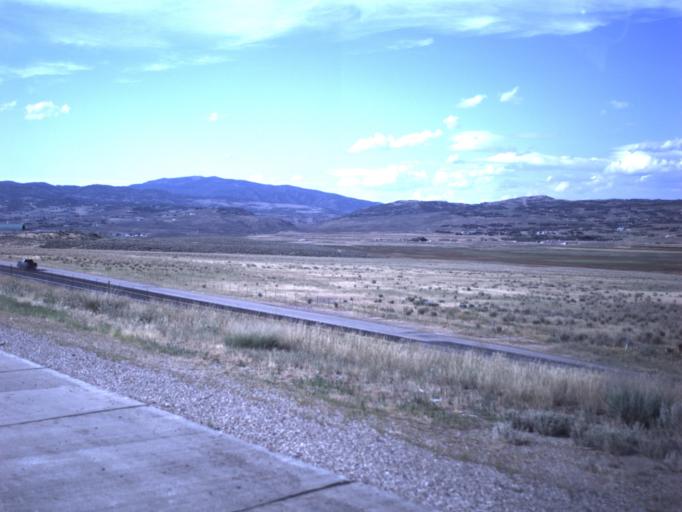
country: US
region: Utah
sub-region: Summit County
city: Park City
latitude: 40.7043
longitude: -111.4764
